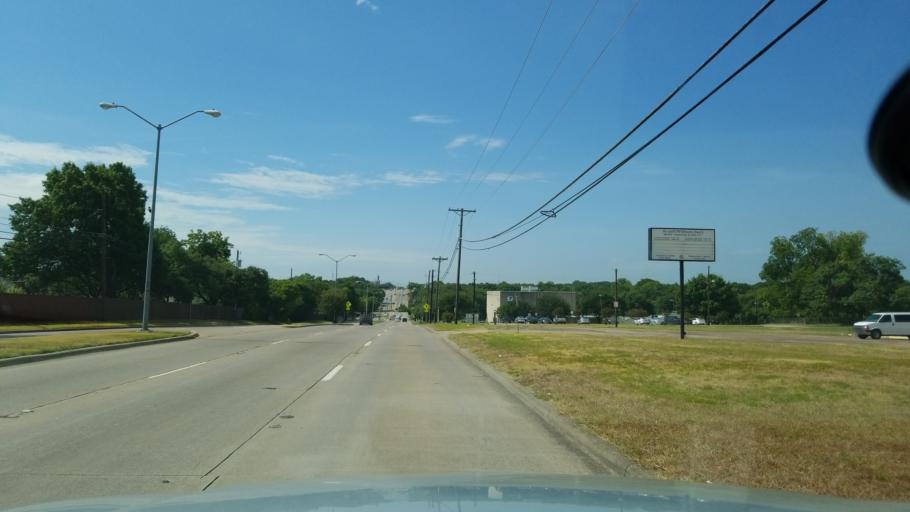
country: US
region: Texas
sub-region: Dallas County
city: Duncanville
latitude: 32.6679
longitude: -96.8572
